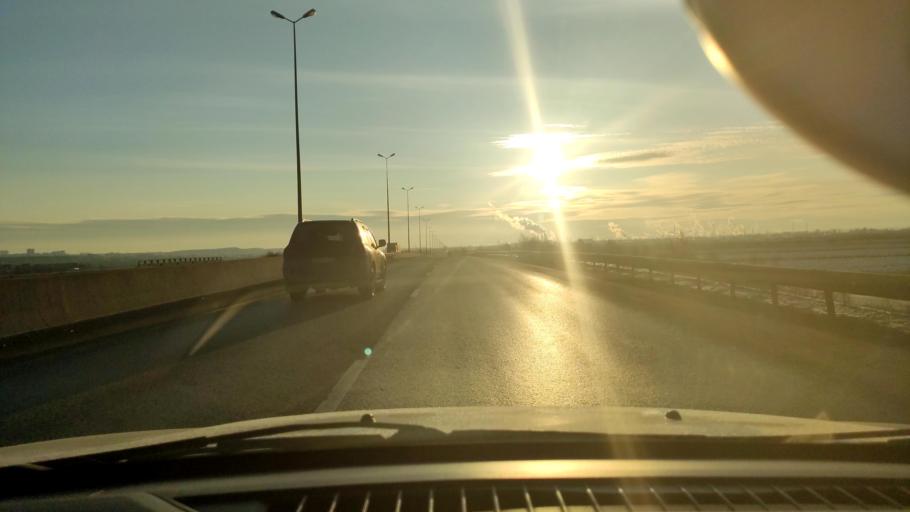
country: RU
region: Perm
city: Kondratovo
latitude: 57.9771
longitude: 56.0821
